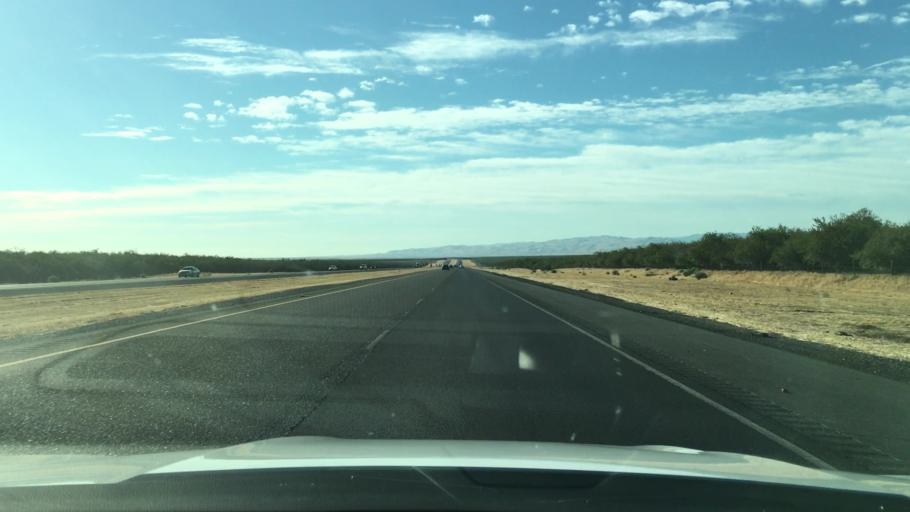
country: US
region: California
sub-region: Merced County
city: South Dos Palos
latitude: 36.7478
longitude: -120.7037
